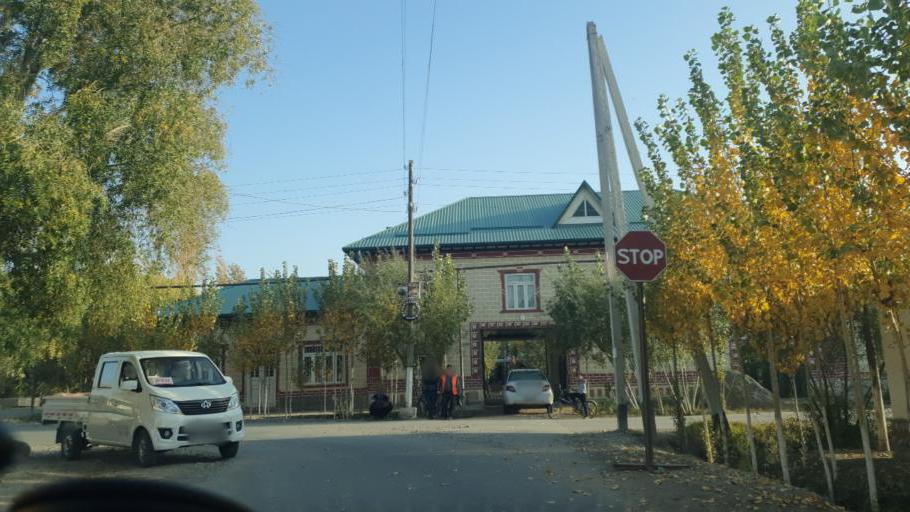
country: UZ
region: Fergana
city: Beshariq
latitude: 40.4622
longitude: 70.5439
